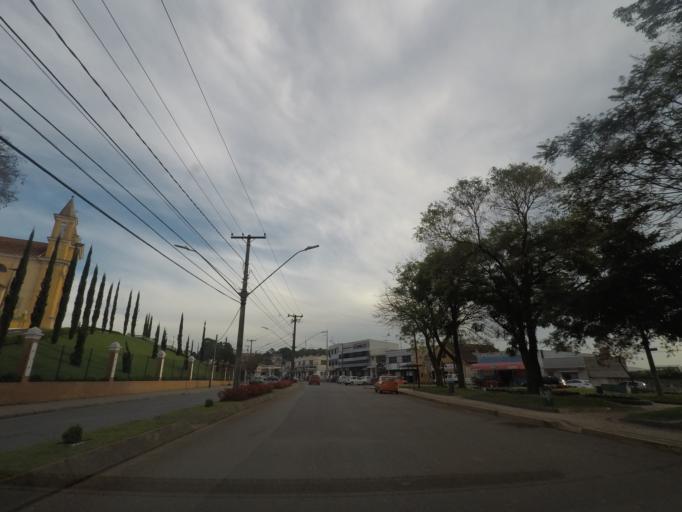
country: BR
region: Parana
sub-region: Colombo
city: Colombo
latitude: -25.2919
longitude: -49.2225
